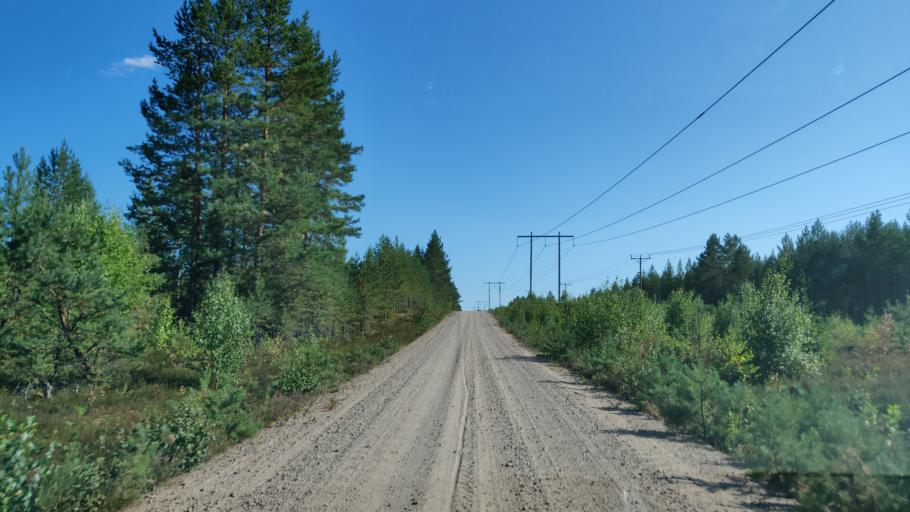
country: SE
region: Vaermland
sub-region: Hagfors Kommun
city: Ekshaerad
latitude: 60.0629
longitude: 13.5203
